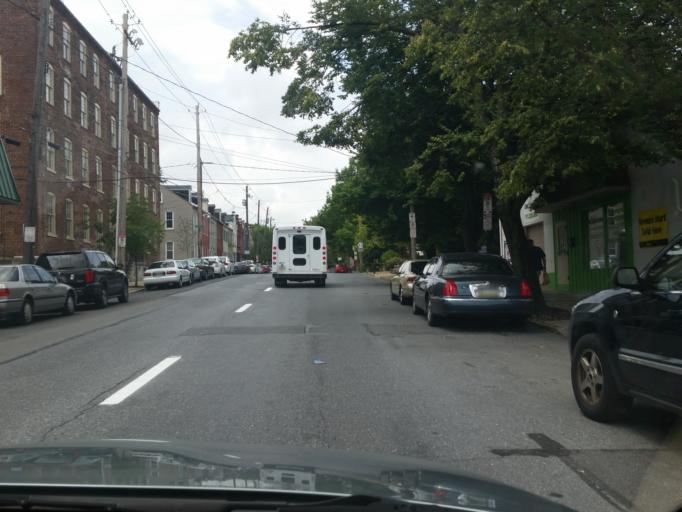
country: US
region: Pennsylvania
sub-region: Lancaster County
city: Lancaster
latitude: 40.0434
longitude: -76.2995
